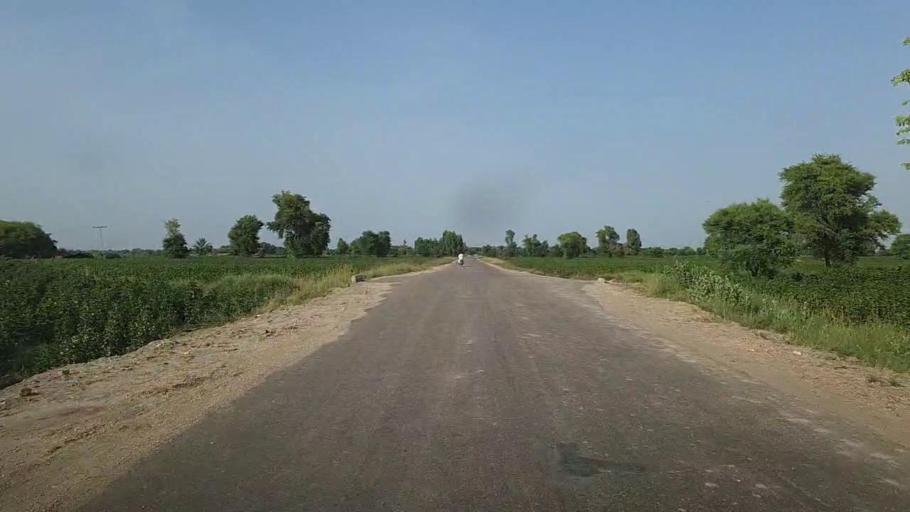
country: PK
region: Sindh
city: Khairpur
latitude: 28.0808
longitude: 69.8346
